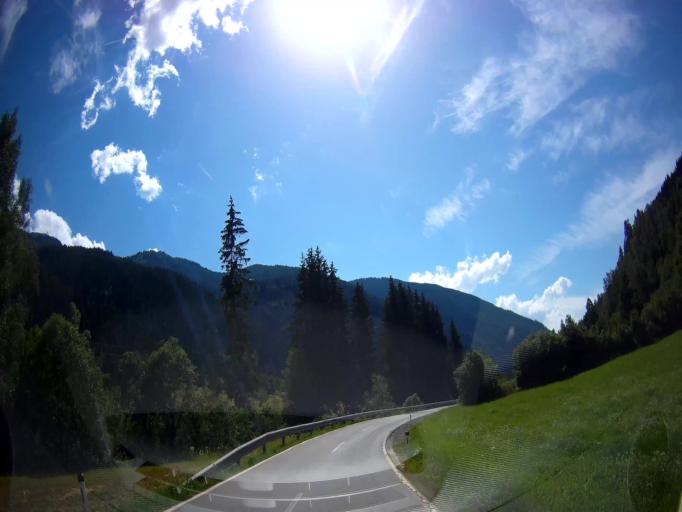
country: AT
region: Salzburg
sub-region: Politischer Bezirk Tamsweg
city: Thomatal
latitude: 47.0633
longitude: 13.7828
